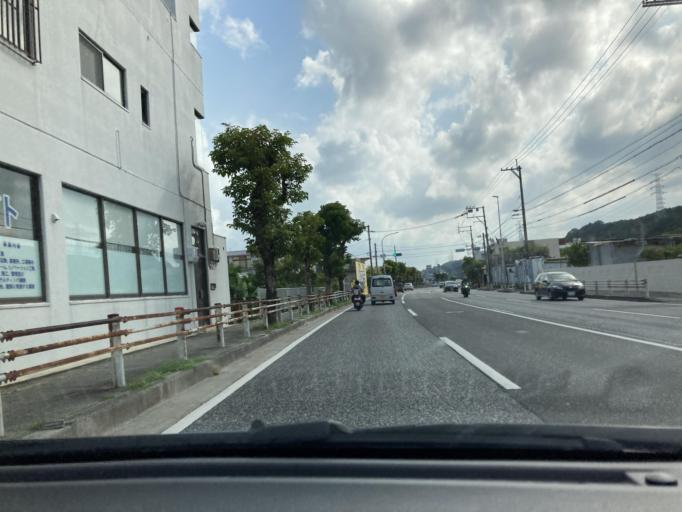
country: JP
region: Okinawa
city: Ginowan
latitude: 26.2648
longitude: 127.7898
